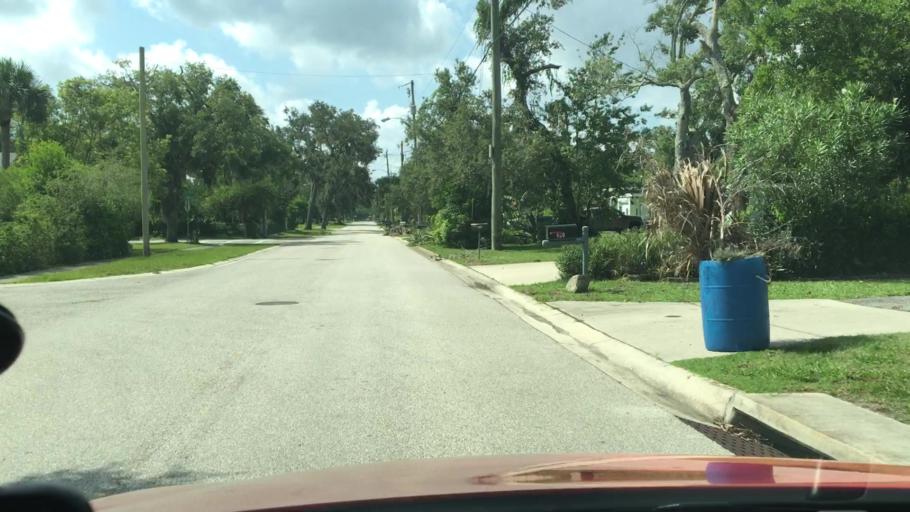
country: US
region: Florida
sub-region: Volusia County
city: Ormond Beach
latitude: 29.2727
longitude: -81.0529
